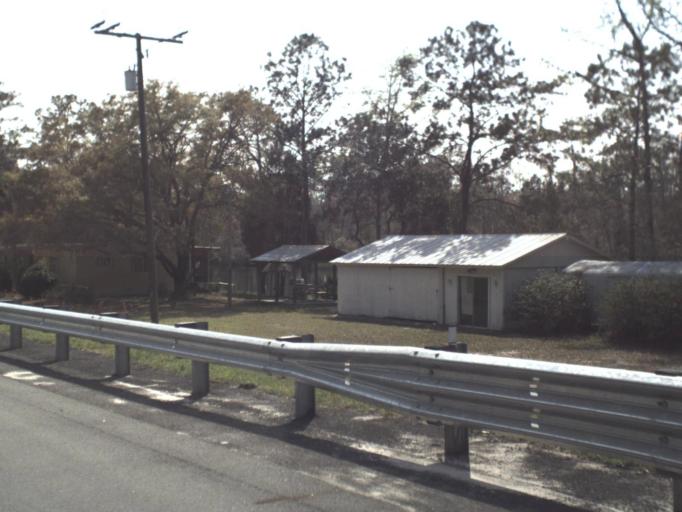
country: US
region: Florida
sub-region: Wakulla County
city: Crawfordville
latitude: 30.0217
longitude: -84.4999
